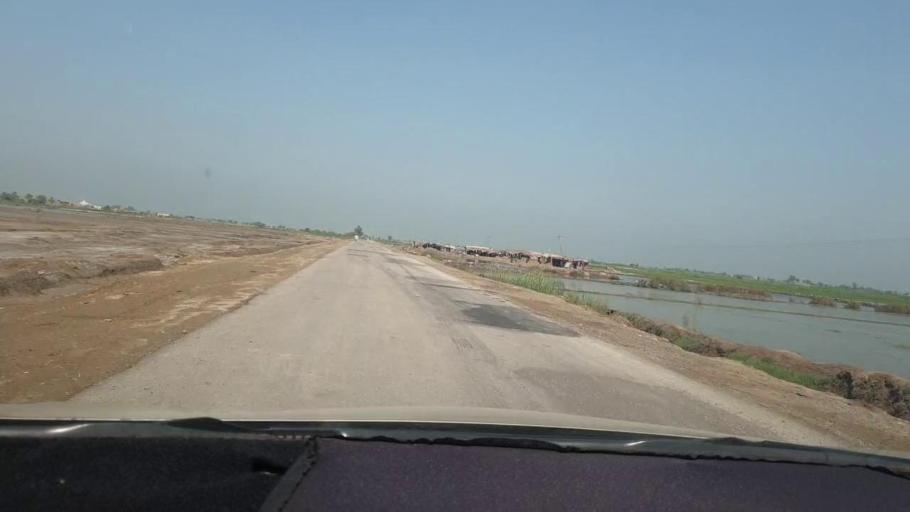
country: PK
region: Sindh
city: Shahdadkot
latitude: 27.8341
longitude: 68.0124
